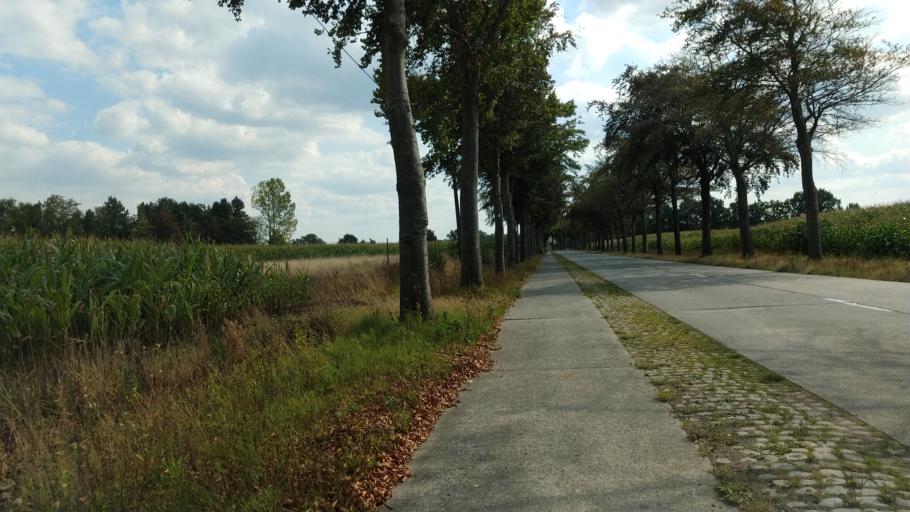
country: BE
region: Flanders
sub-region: Provincie Oost-Vlaanderen
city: Assenede
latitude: 51.2049
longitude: 3.6847
